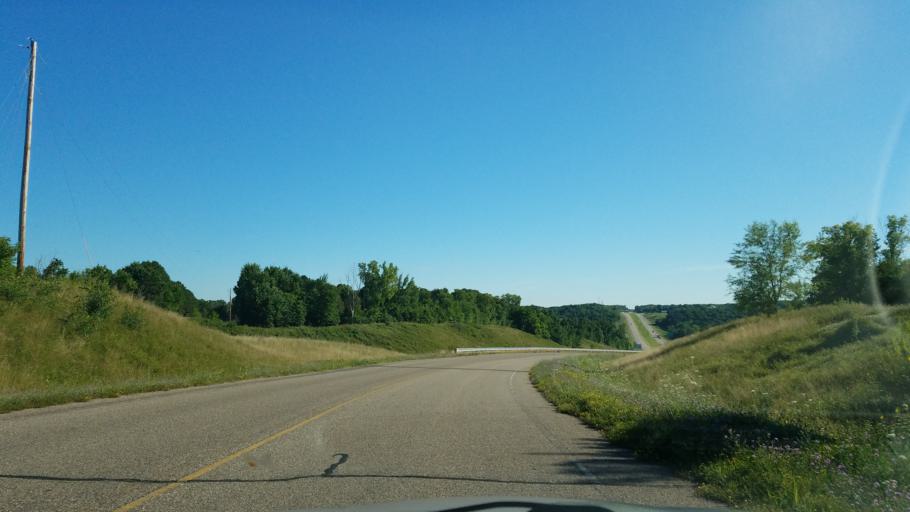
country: US
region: Wisconsin
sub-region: Saint Croix County
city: Somerset
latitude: 45.1076
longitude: -92.7269
